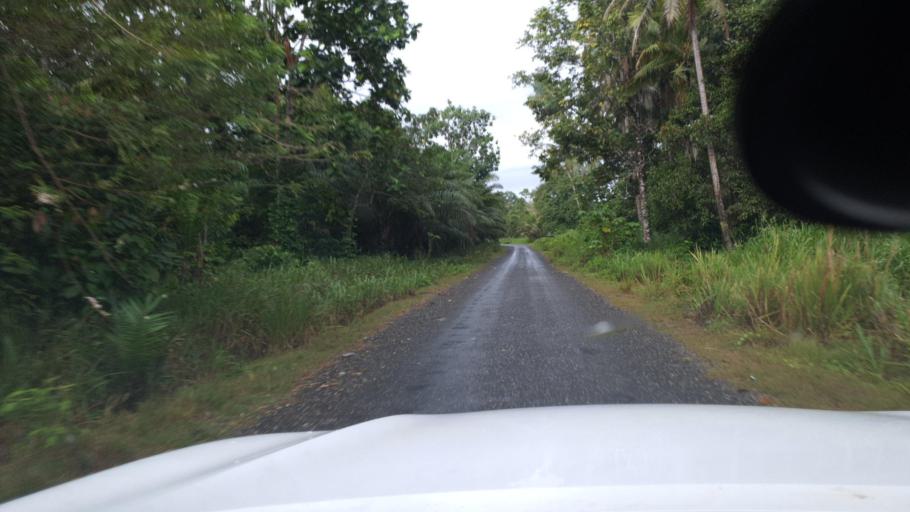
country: SB
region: Guadalcanal
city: Honiara
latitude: -9.4801
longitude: 160.3578
